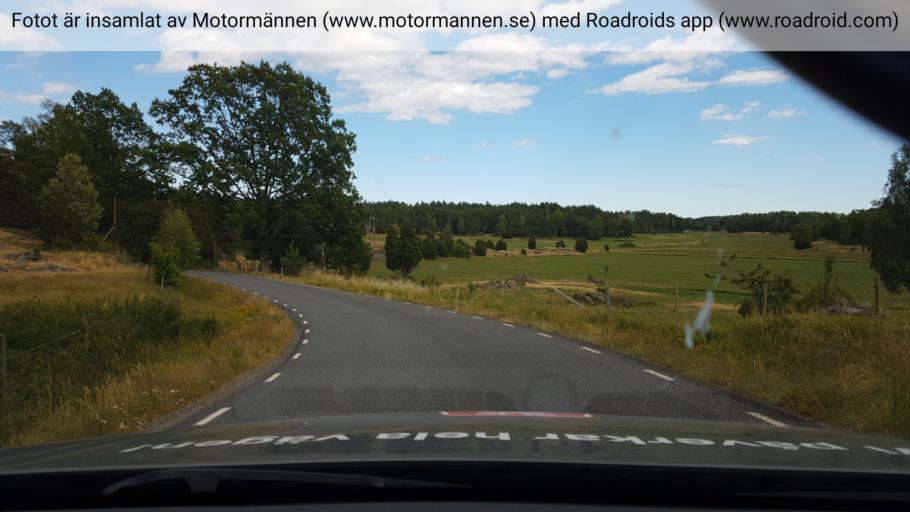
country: SE
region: Kalmar
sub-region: Vasterviks Kommun
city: Forserum
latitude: 57.9474
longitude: 16.6492
